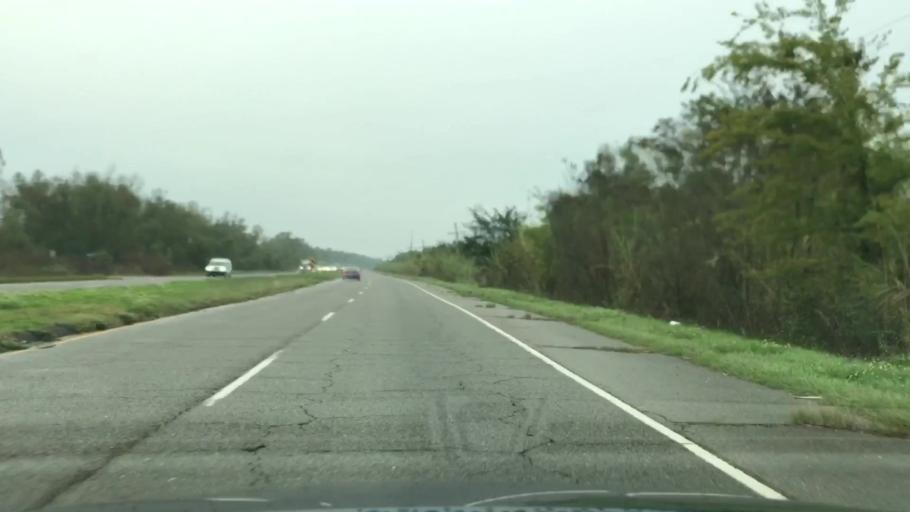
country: US
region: Louisiana
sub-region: Saint Charles Parish
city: Des Allemands
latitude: 29.7952
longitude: -90.5089
